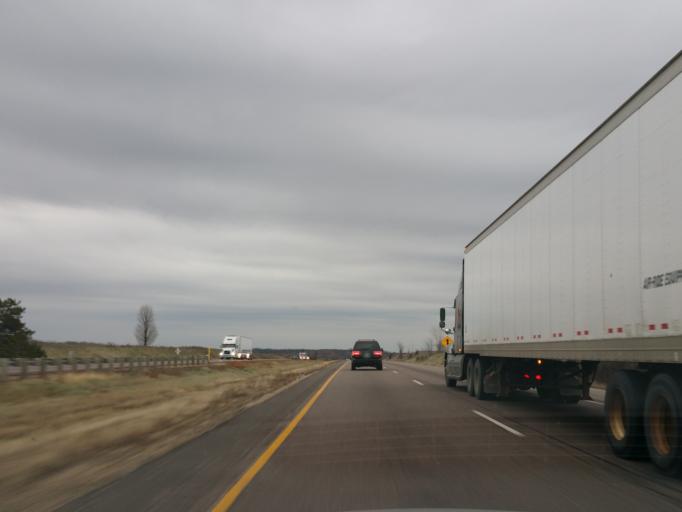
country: US
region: Wisconsin
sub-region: Dunn County
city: Boyceville
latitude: 44.9207
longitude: -92.1158
